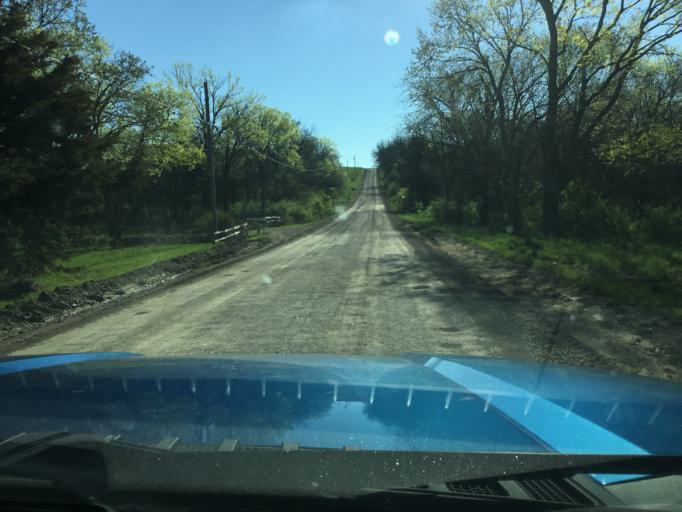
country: US
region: Kansas
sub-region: Douglas County
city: Lawrence
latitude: 38.9569
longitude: -95.3512
